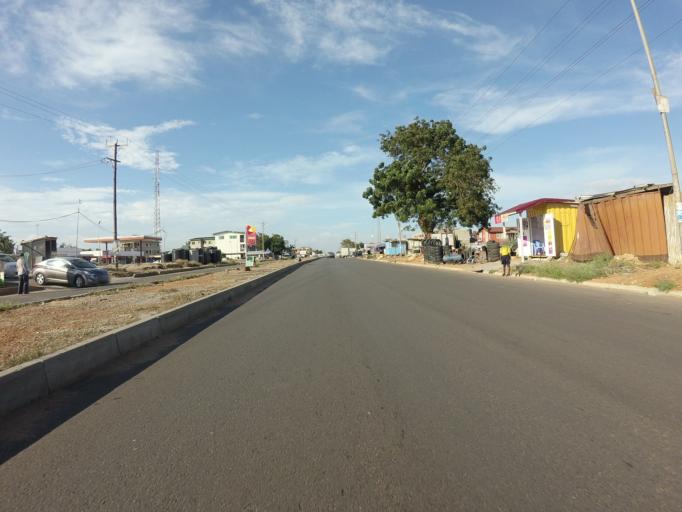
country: GH
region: Greater Accra
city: Nungua
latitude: 5.6261
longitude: -0.0682
